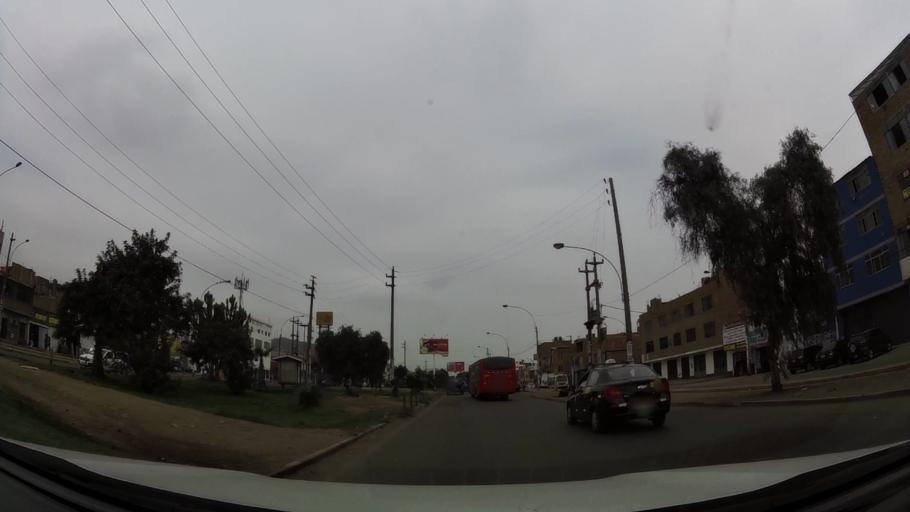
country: PE
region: Lima
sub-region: Lima
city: Independencia
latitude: -12.0099
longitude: -77.0814
